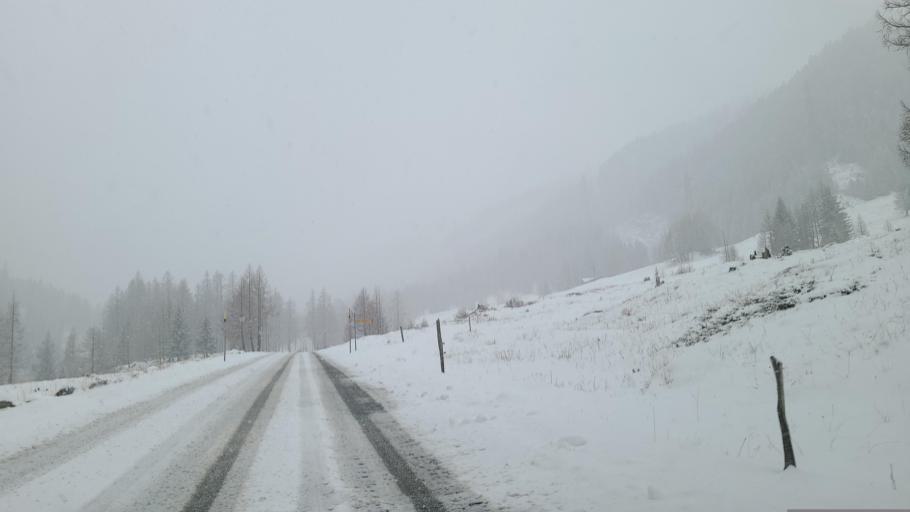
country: CH
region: Ticino
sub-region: Leventina District
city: Airolo
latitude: 46.4919
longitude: 8.4880
